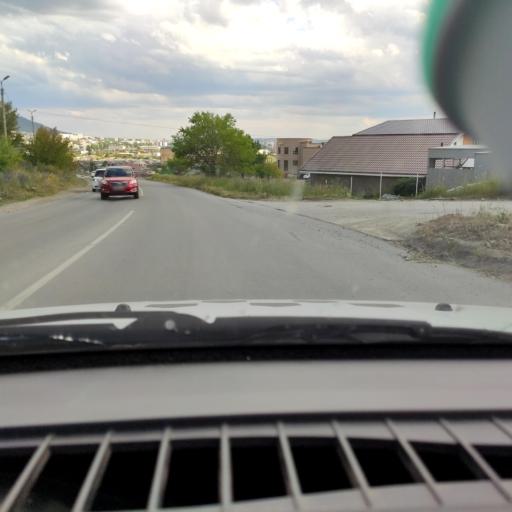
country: RU
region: Chelyabinsk
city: Miass
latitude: 55.0772
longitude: 60.0933
